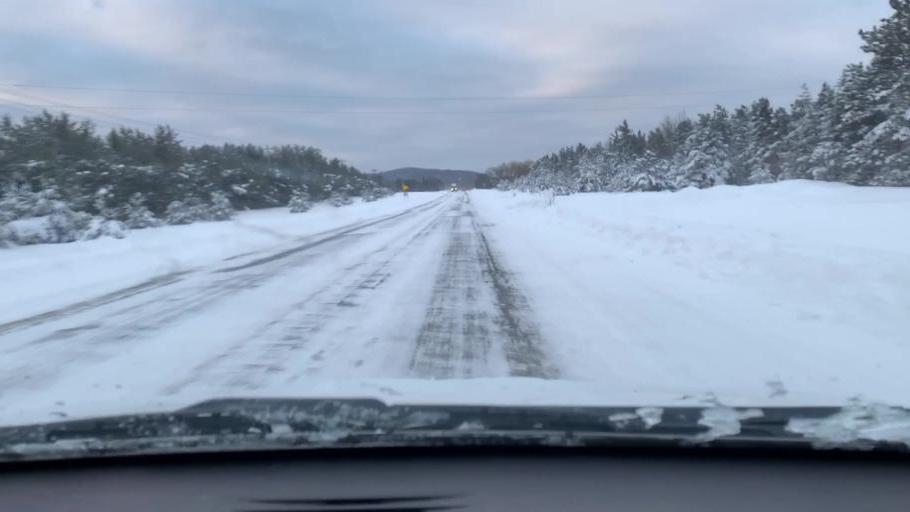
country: US
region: Michigan
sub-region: Antrim County
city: Mancelona
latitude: 44.9208
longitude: -85.0510
